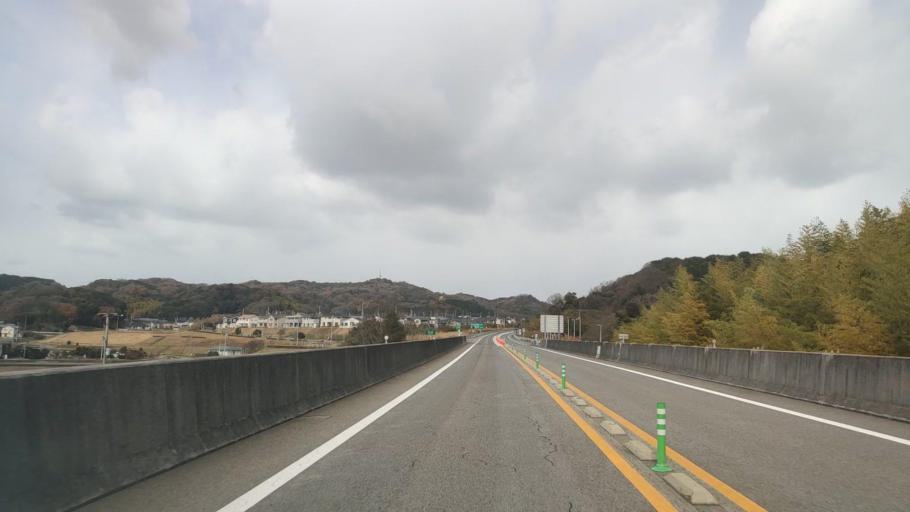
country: JP
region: Ehime
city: Hojo
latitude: 34.0639
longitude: 132.9732
